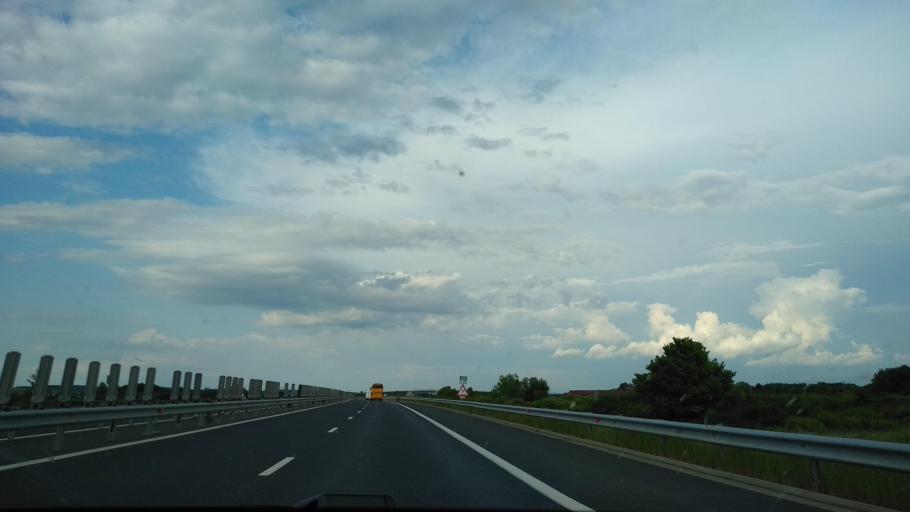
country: RO
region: Timis
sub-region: Comuna Bethausen
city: Bethausen
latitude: 45.8567
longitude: 21.9714
